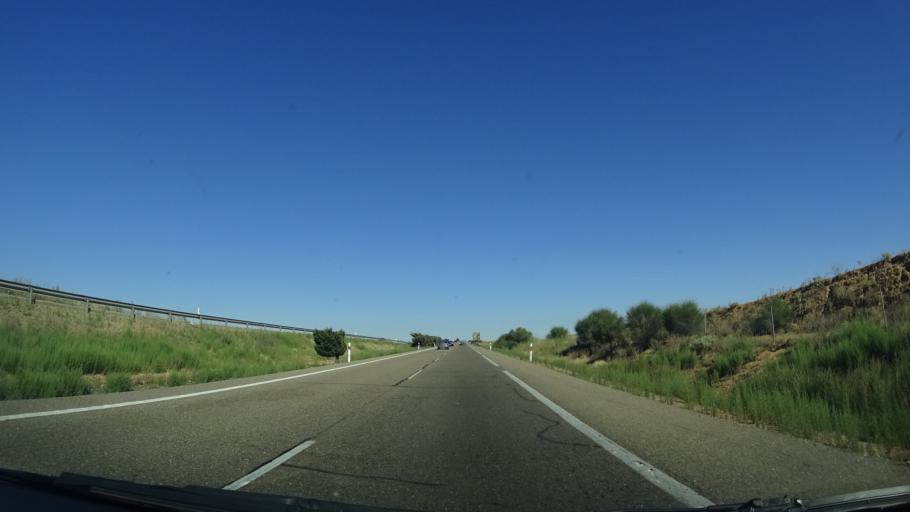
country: ES
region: Castille and Leon
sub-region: Provincia de Zamora
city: San Esteban del Molar
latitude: 41.9272
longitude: -5.5292
